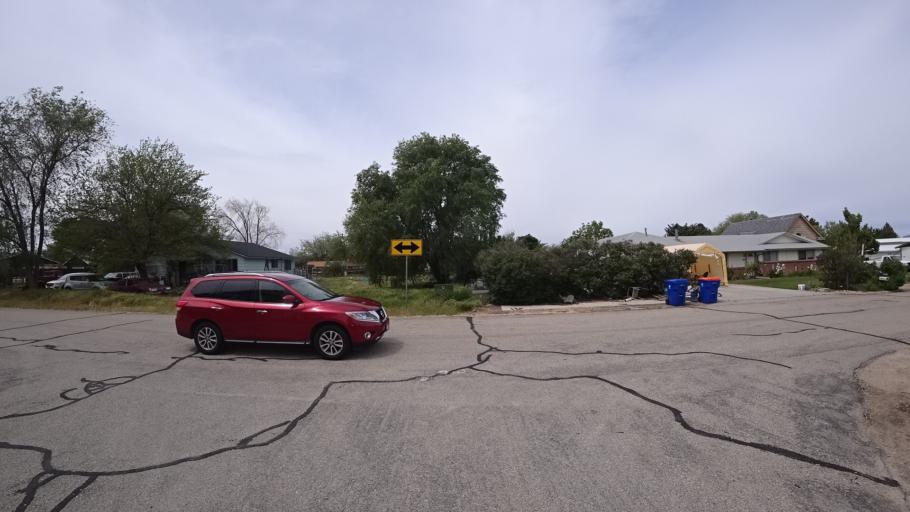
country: US
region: Idaho
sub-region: Ada County
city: Meridian
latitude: 43.5329
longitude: -116.3185
